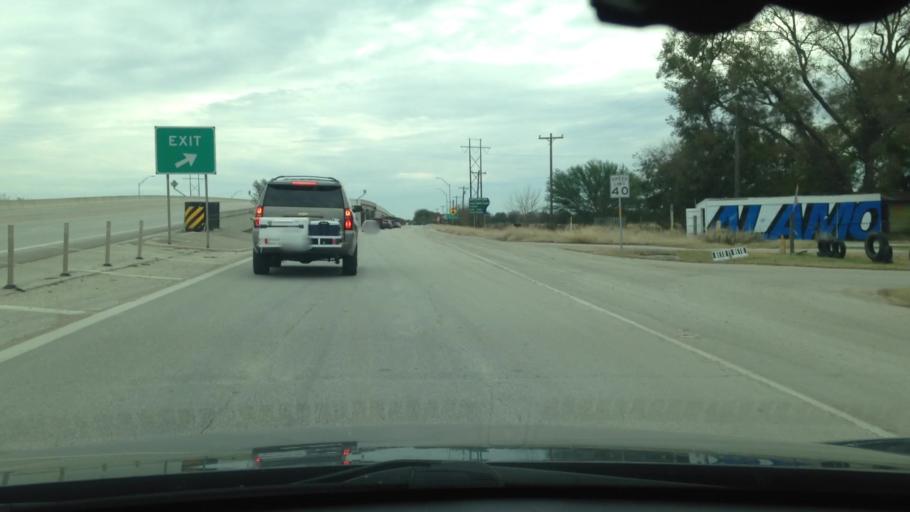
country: US
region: Texas
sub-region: Hays County
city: San Marcos
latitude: 29.8783
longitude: -97.9083
